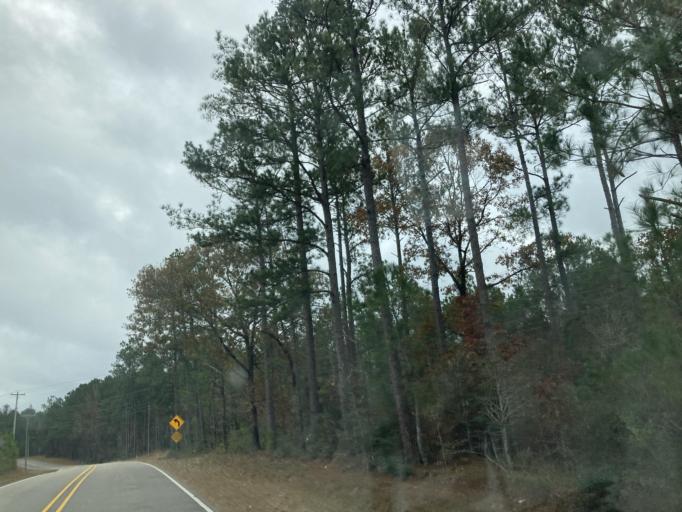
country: US
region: Mississippi
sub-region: Lamar County
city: Lumberton
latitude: 31.0658
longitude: -89.6147
